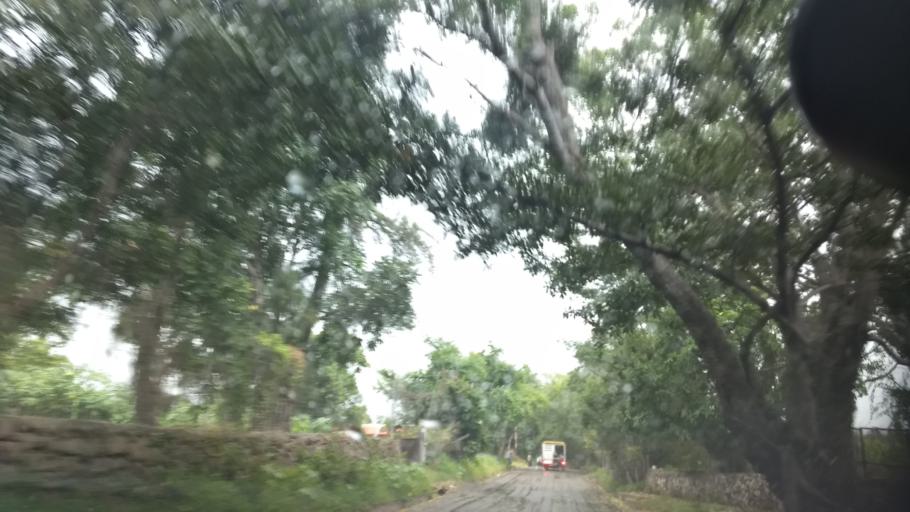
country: MX
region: Jalisco
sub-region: Tonila
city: San Marcos
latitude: 19.4424
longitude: -103.4953
